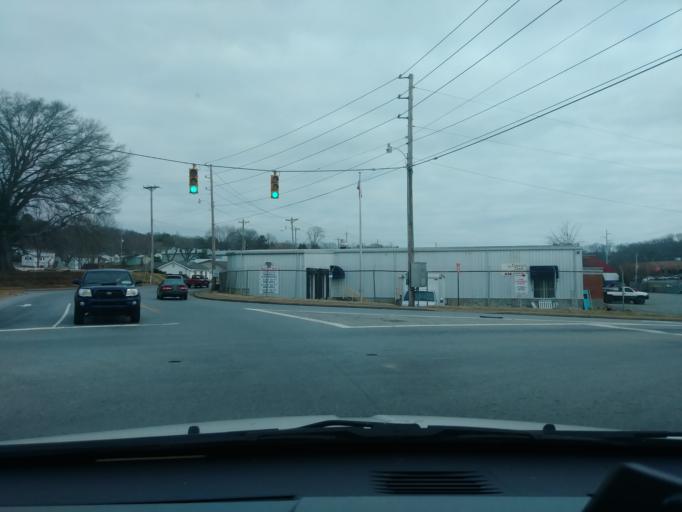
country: US
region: Tennessee
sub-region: Greene County
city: Greeneville
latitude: 36.1616
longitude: -82.8199
